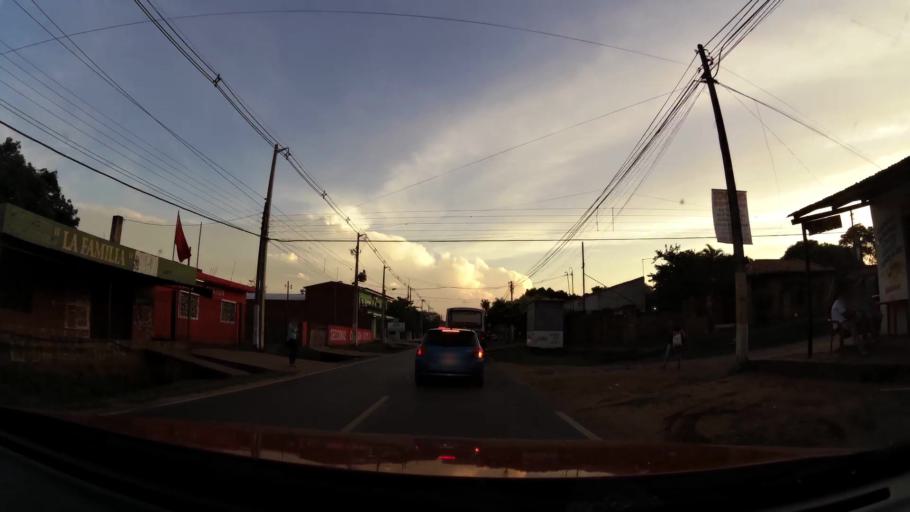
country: PY
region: Central
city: San Lorenzo
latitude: -25.3771
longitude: -57.4926
